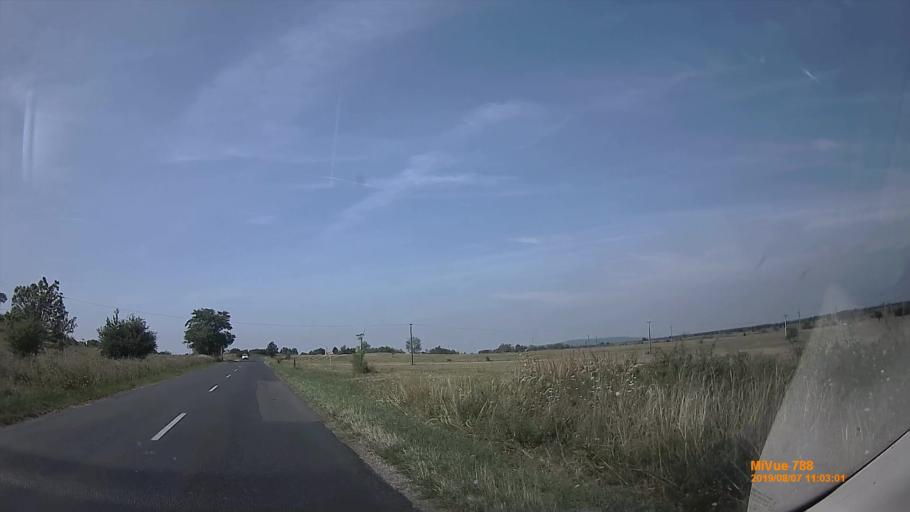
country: HU
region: Veszprem
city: Ajka
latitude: 47.0259
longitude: 17.5173
